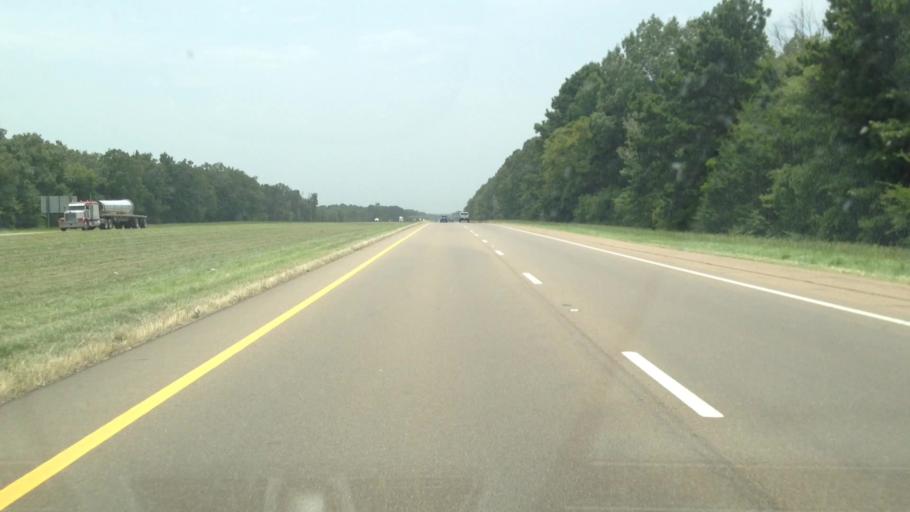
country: US
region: Texas
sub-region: Bowie County
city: De Kalb
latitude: 33.4118
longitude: -94.5632
